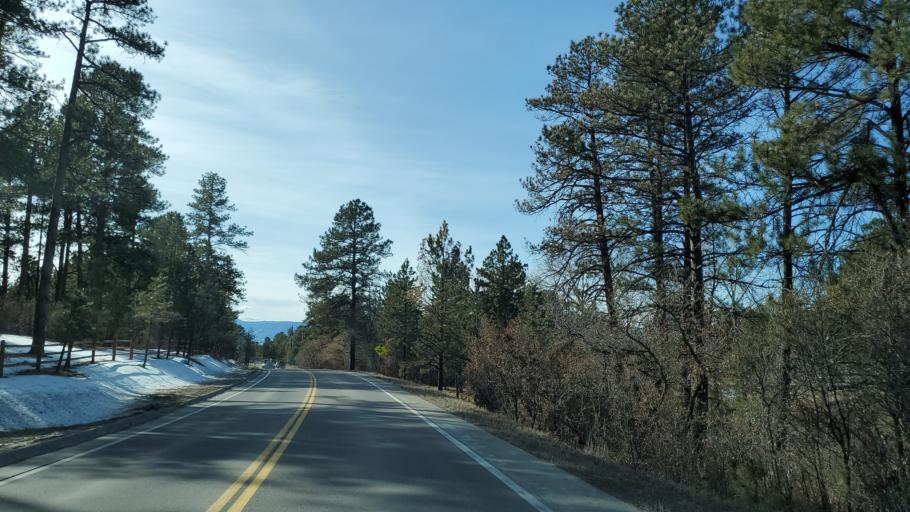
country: US
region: Colorado
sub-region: Douglas County
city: Castle Pines
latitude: 39.4421
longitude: -104.8849
